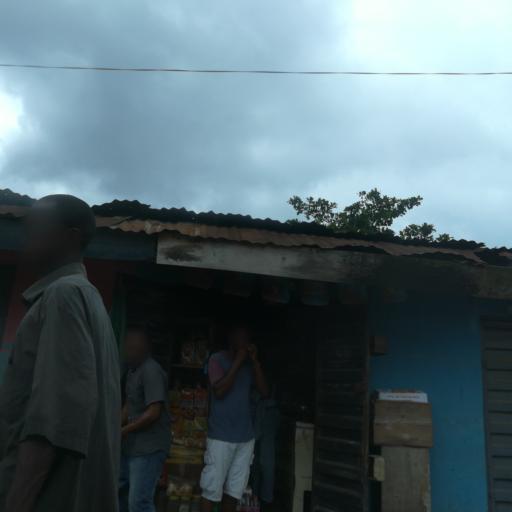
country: NG
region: Lagos
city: Agege
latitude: 6.6040
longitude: 3.2969
